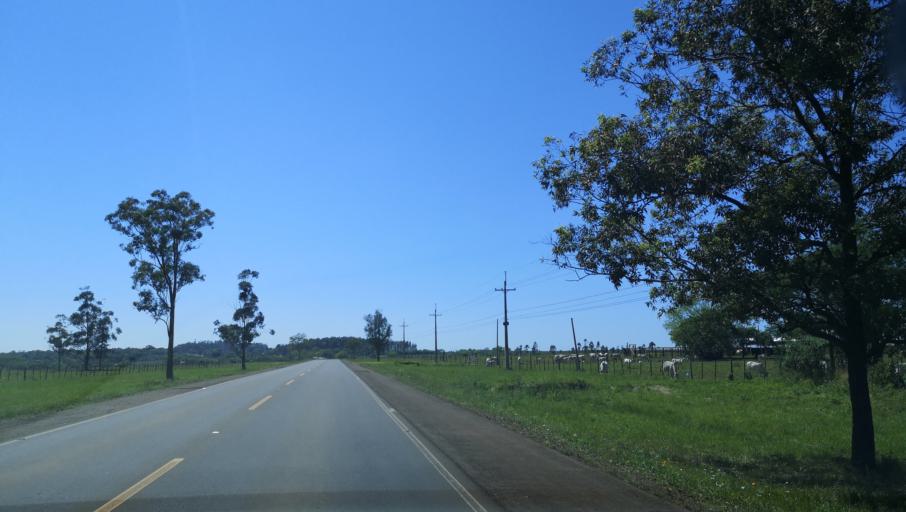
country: PY
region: Itapua
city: Carmen del Parana
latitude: -27.2210
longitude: -56.1097
